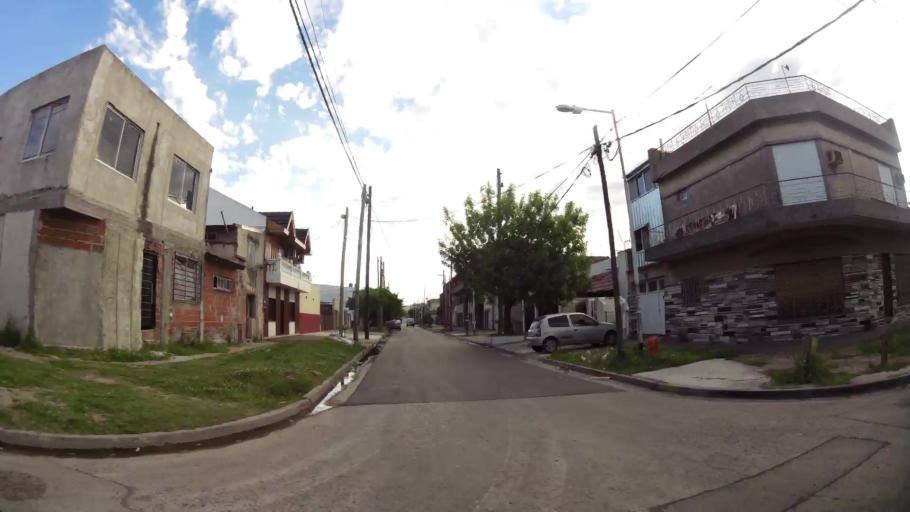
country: AR
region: Buenos Aires
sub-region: Partido de Avellaneda
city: Avellaneda
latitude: -34.6843
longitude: -58.3571
